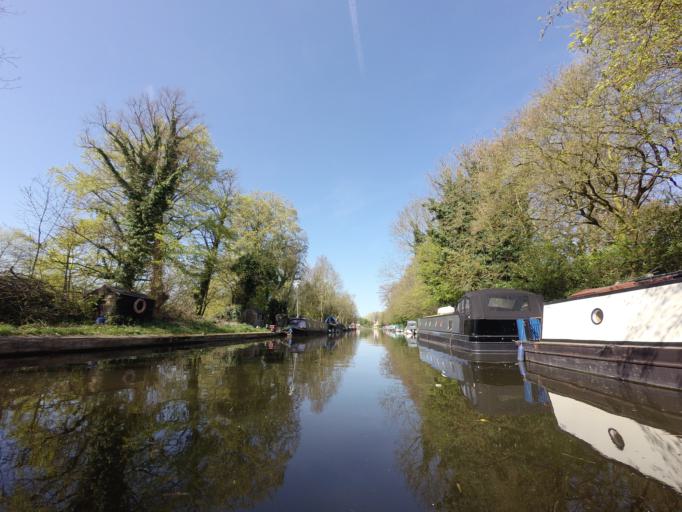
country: GB
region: England
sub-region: Greater London
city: Uxbridge
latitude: 51.5266
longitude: -0.4862
